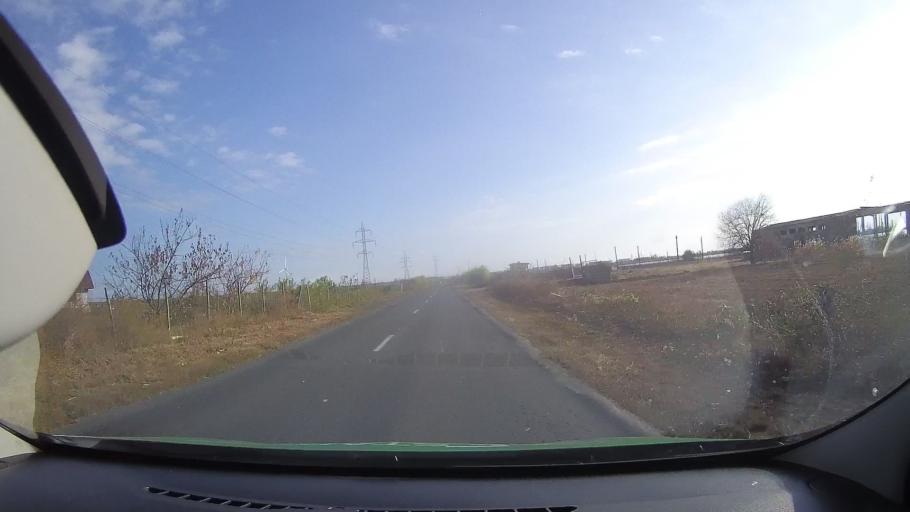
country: RO
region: Constanta
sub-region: Comuna Corbu
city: Corbu
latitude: 44.3691
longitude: 28.6690
